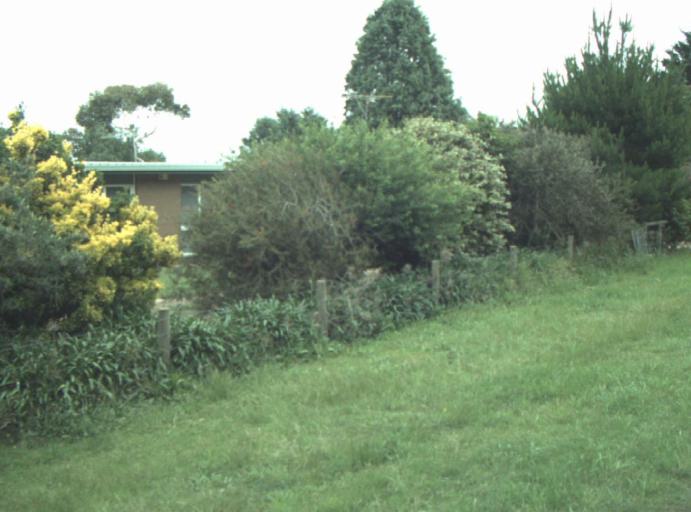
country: AU
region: Victoria
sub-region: Greater Geelong
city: Bell Post Hill
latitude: -38.0547
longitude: 144.3178
